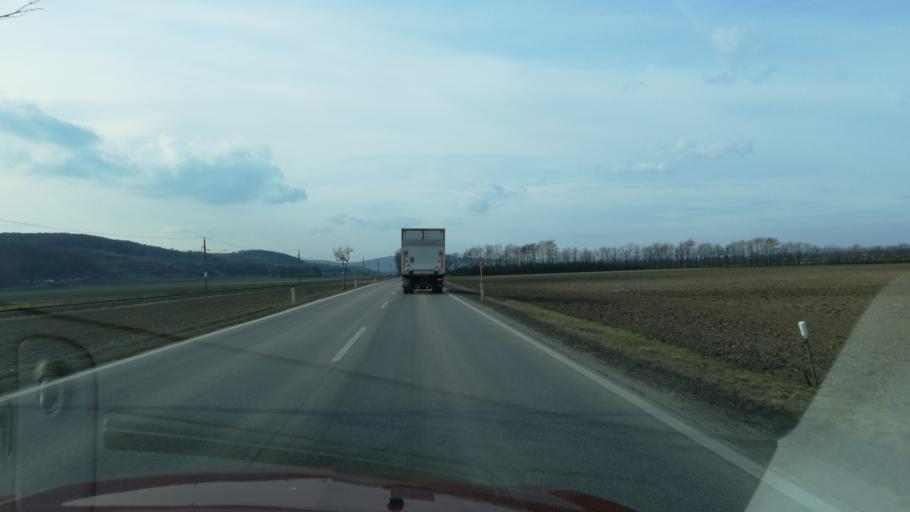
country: AT
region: Lower Austria
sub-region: Politischer Bezirk Tulln
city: Grafenworth
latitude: 48.3384
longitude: 15.7976
